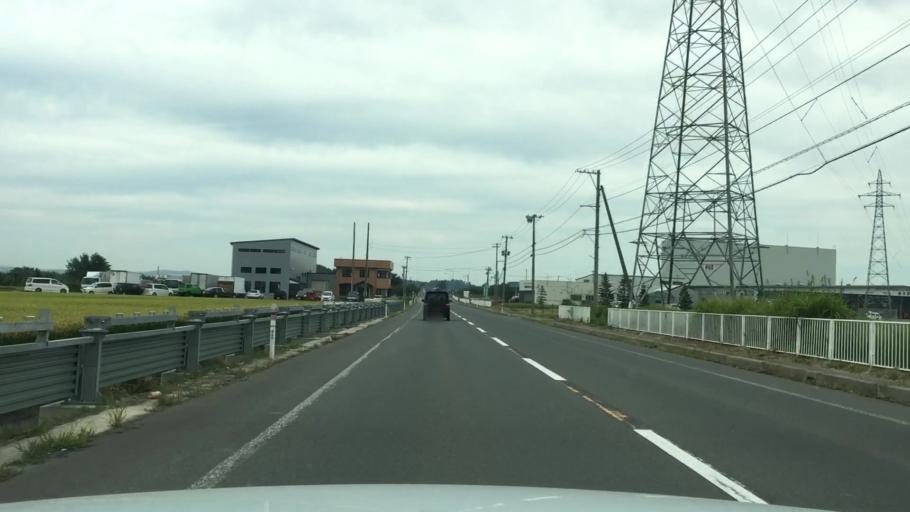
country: JP
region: Aomori
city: Hirosaki
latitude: 40.6343
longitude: 140.4500
